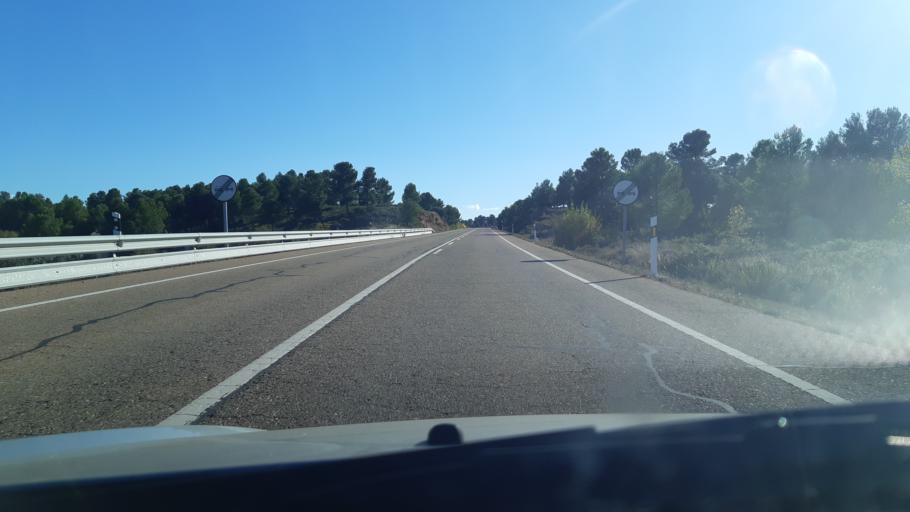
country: ES
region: Aragon
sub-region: Provincia de Teruel
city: Valjunquera
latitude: 40.9378
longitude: -0.0111
